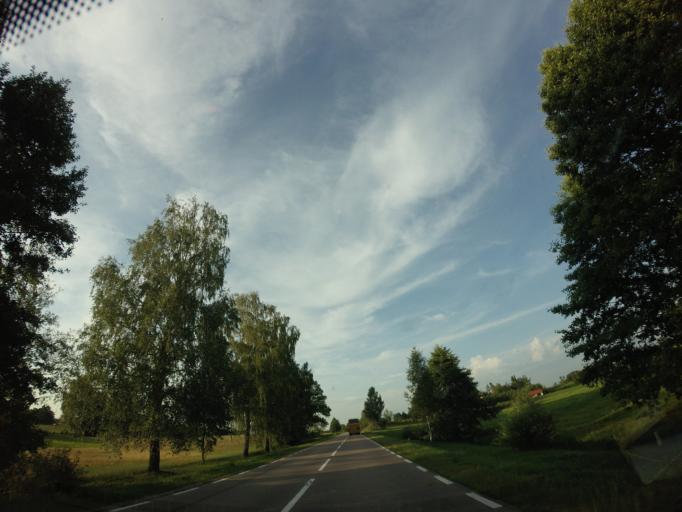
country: PL
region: Podlasie
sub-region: Powiat sejnenski
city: Sejny
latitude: 54.0687
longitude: 23.3633
